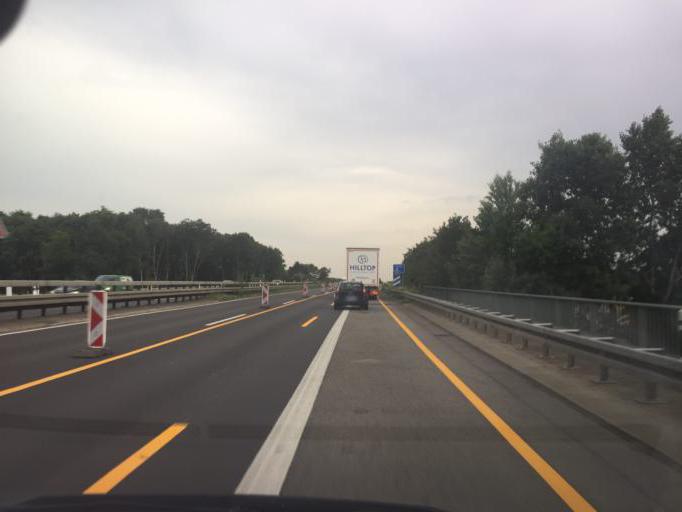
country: DE
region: North Rhine-Westphalia
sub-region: Regierungsbezirk Dusseldorf
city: Viersen
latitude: 51.2568
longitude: 6.3618
